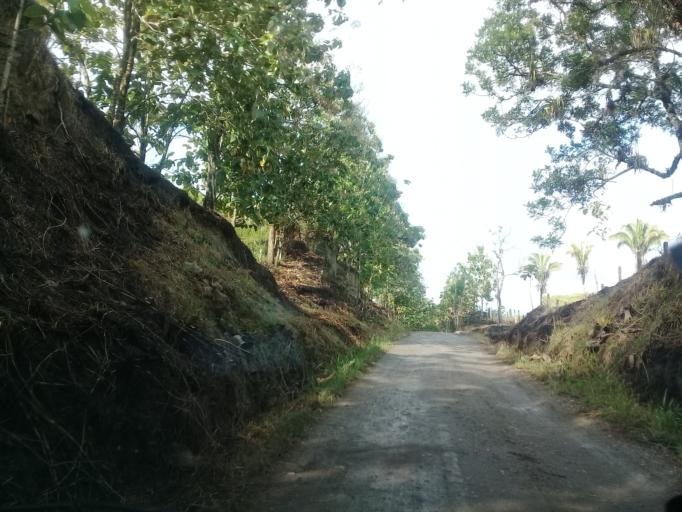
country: CO
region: Antioquia
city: Puerto Triunfo
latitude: 5.7227
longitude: -74.5289
